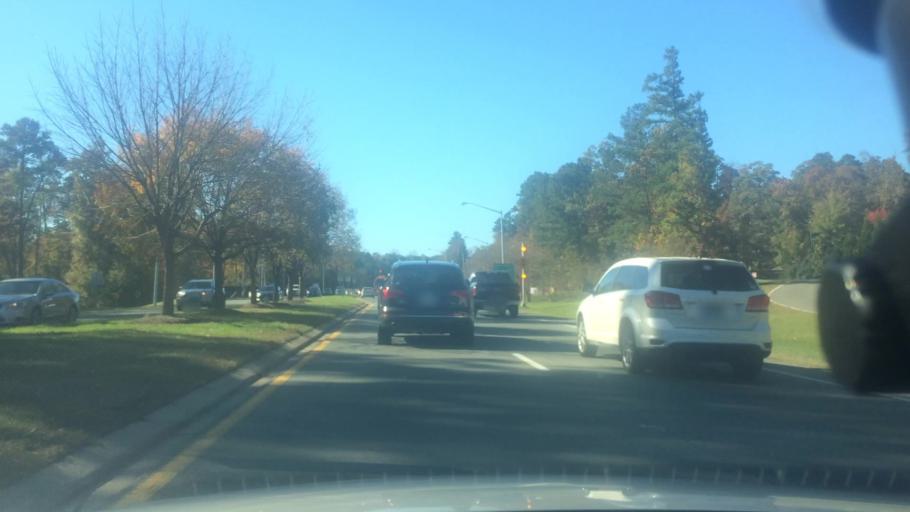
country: US
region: North Carolina
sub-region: Orange County
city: Chapel Hill
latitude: 35.9028
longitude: -79.0318
